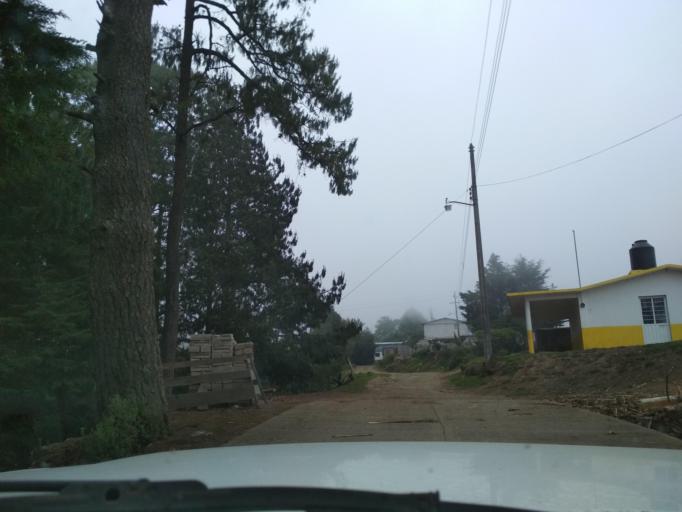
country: MX
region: Veracruz
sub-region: Mariano Escobedo
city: San Isidro el Berro
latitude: 18.9298
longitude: -97.2176
